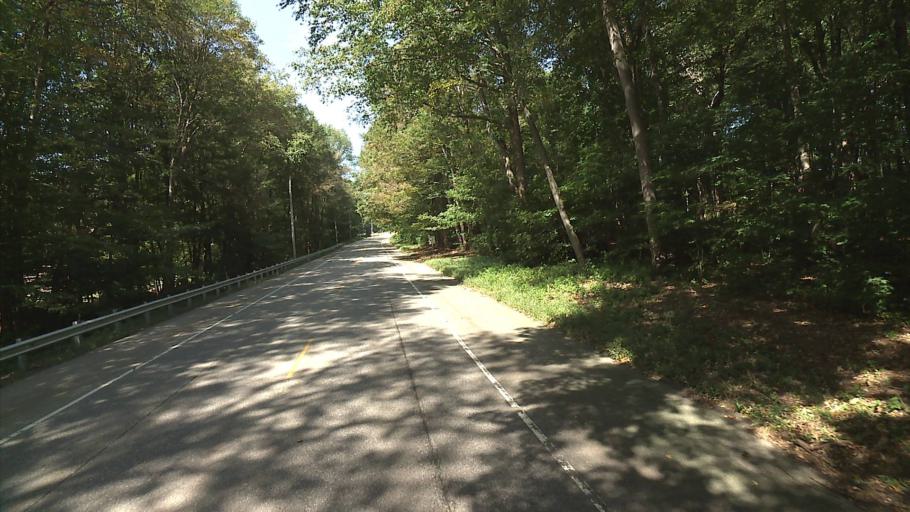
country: US
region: Connecticut
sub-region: New London County
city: Baltic
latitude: 41.5922
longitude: -72.1608
